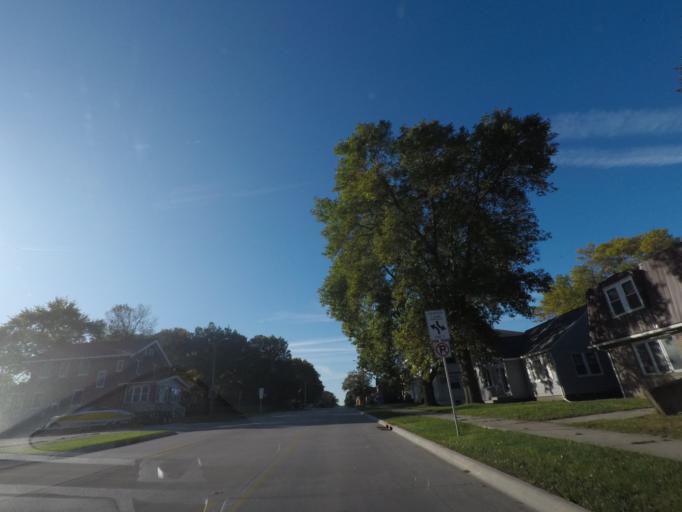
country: US
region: Iowa
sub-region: Story County
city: Nevada
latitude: 42.0192
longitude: -93.4523
